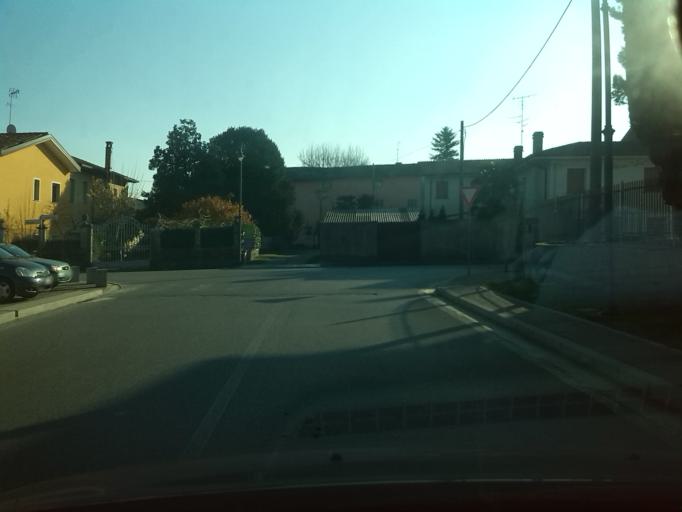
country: IT
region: Friuli Venezia Giulia
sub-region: Provincia di Udine
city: Santa Maria la Longa
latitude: 45.9344
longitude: 13.2948
